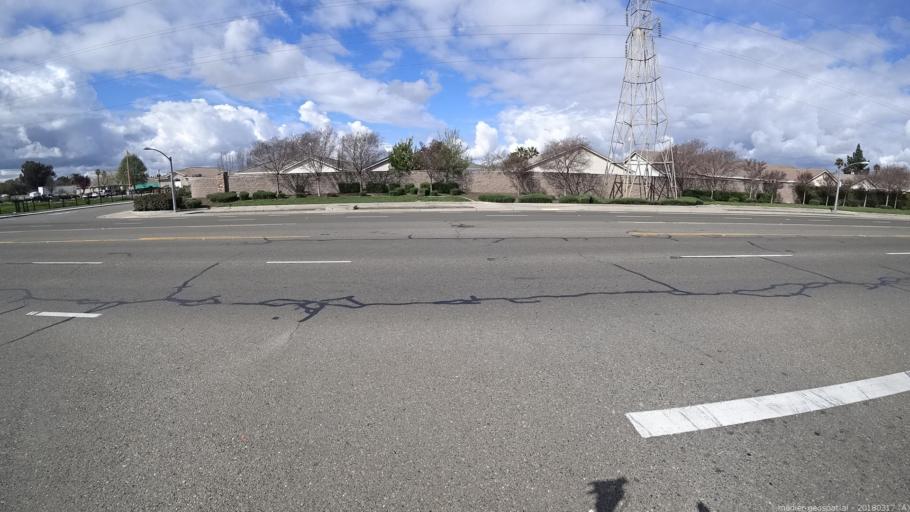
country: US
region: California
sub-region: Sacramento County
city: Florin
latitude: 38.4674
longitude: -121.4086
